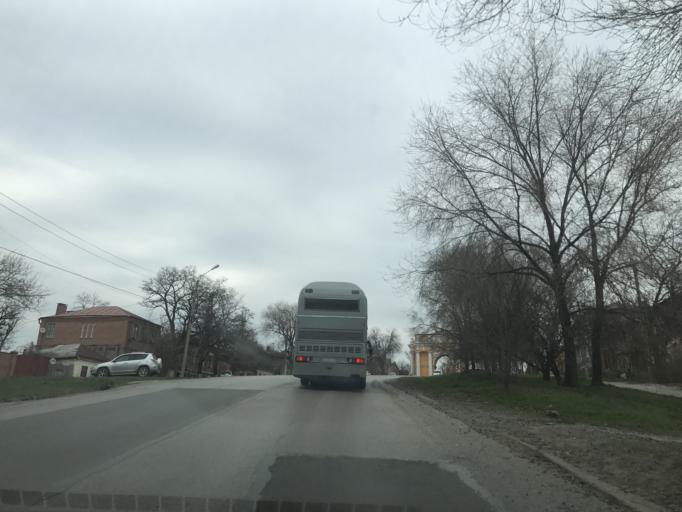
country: RU
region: Rostov
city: Novocherkassk
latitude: 47.4041
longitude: 40.0824
